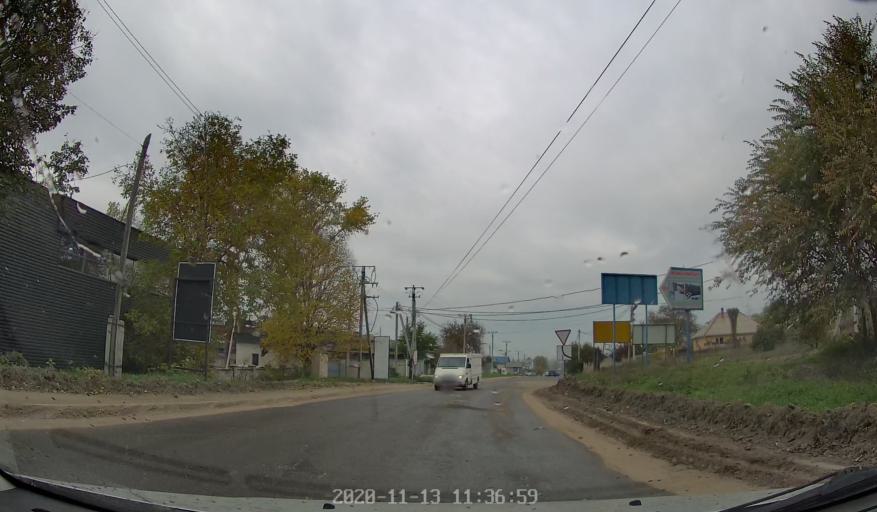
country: MD
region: Chisinau
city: Chisinau
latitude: 46.9898
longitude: 28.9144
